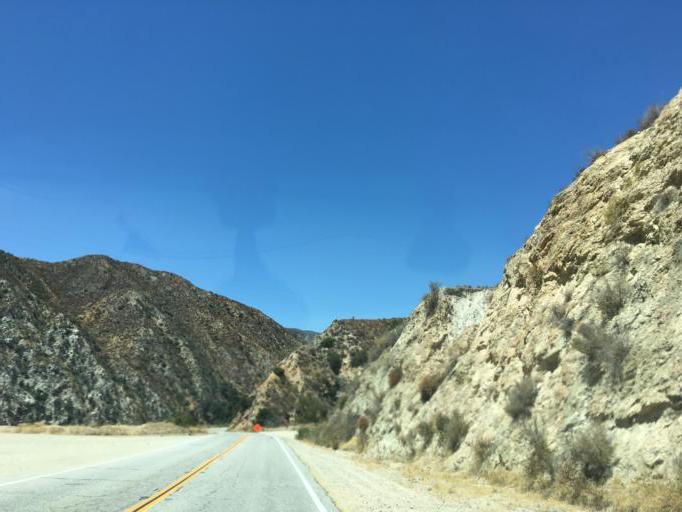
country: US
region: California
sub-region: Los Angeles County
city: La Crescenta-Montrose
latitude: 34.2977
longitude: -118.2443
